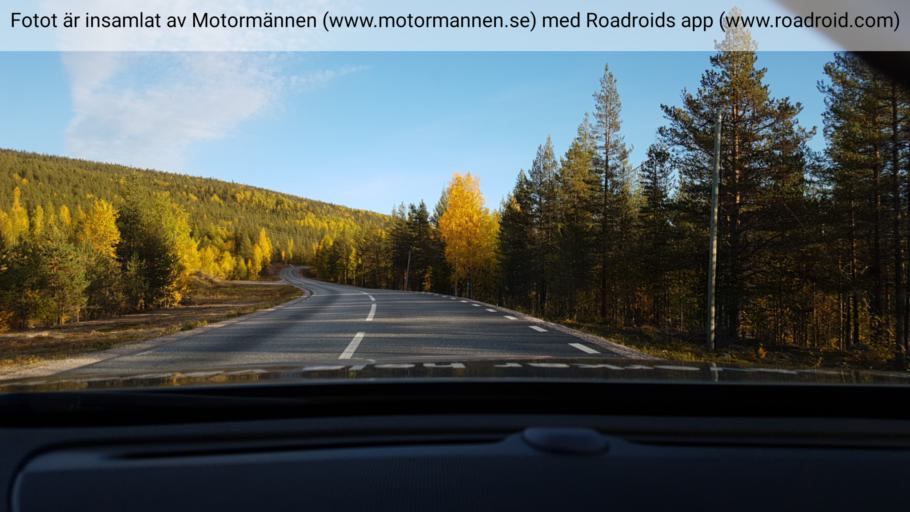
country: SE
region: Norrbotten
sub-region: Jokkmokks Kommun
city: Jokkmokk
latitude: 66.8492
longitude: 19.8255
